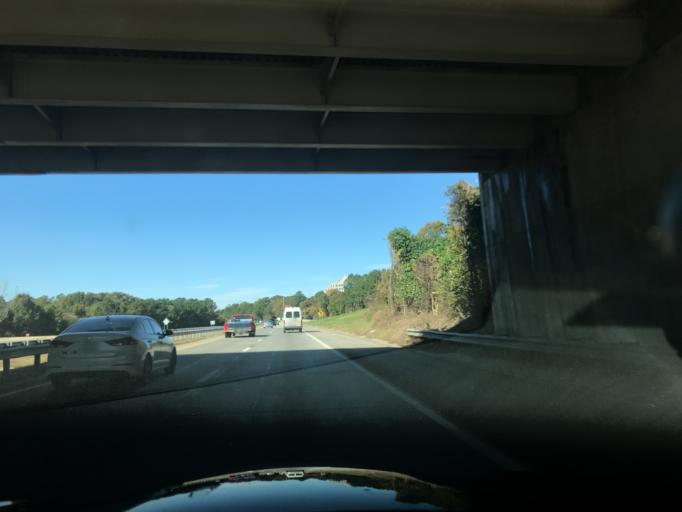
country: US
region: North Carolina
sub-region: Durham County
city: Durham
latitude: 36.0037
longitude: -78.9203
